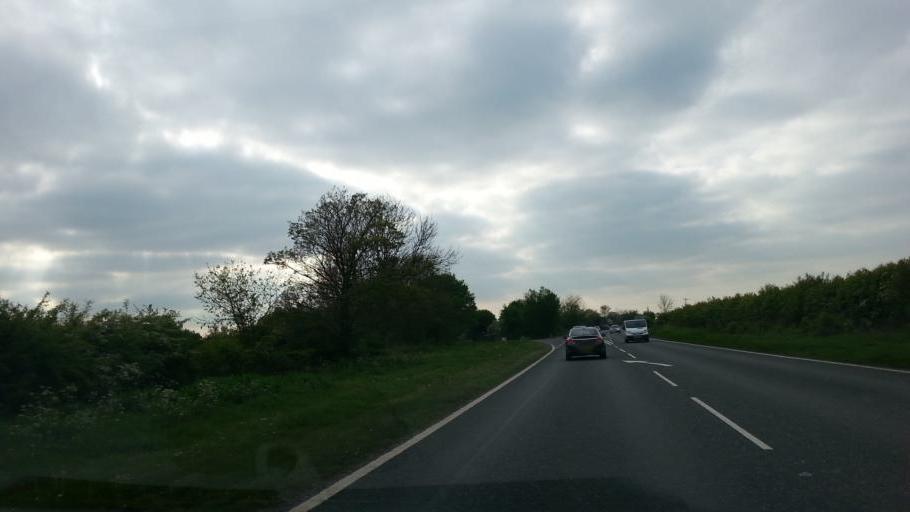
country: GB
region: England
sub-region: Nottinghamshire
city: South Collingham
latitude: 53.0719
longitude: -0.6835
